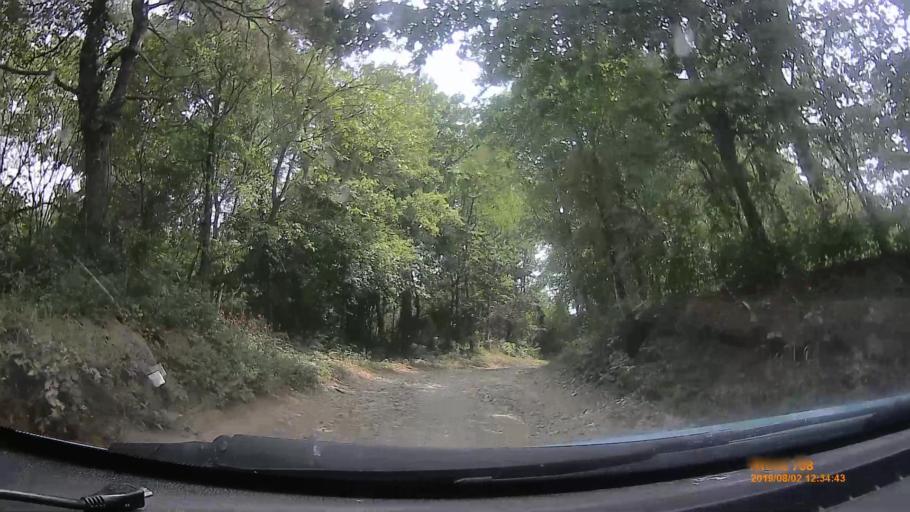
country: HU
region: Baranya
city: Buekkoesd
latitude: 46.0988
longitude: 17.9479
